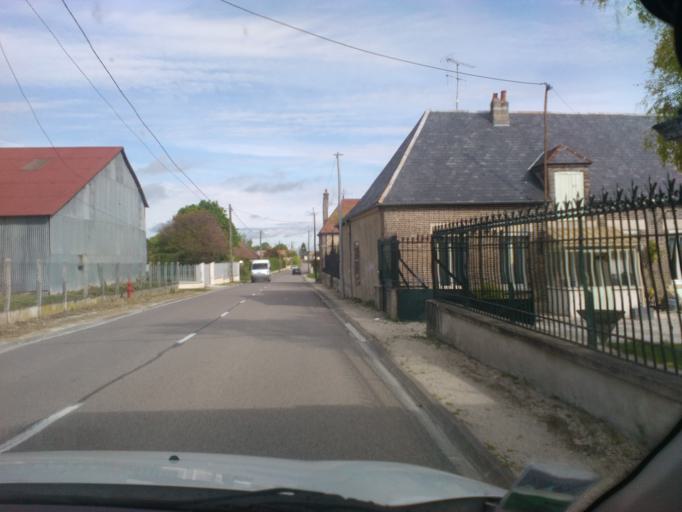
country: FR
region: Champagne-Ardenne
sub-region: Departement de l'Aube
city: Marigny-le-Chatel
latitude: 48.3880
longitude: 3.8322
